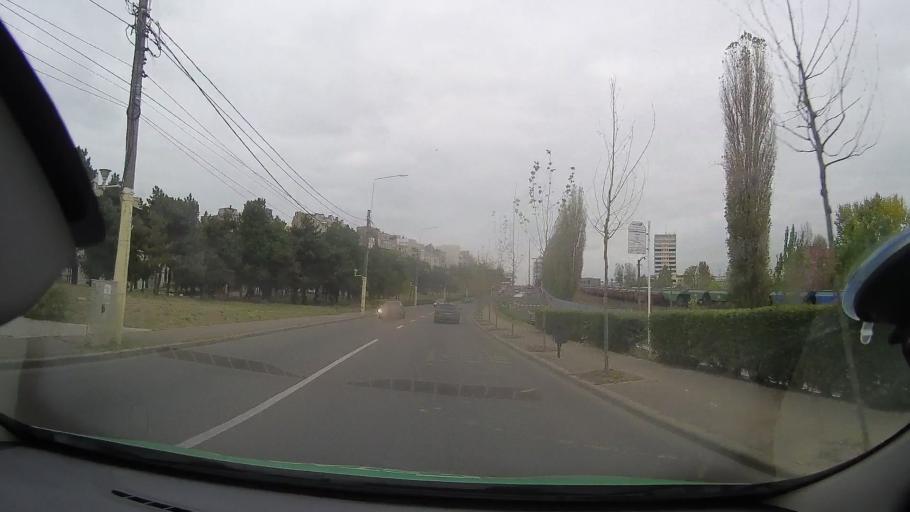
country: RO
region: Constanta
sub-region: Municipiul Constanta
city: Constanta
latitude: 44.1732
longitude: 28.6570
